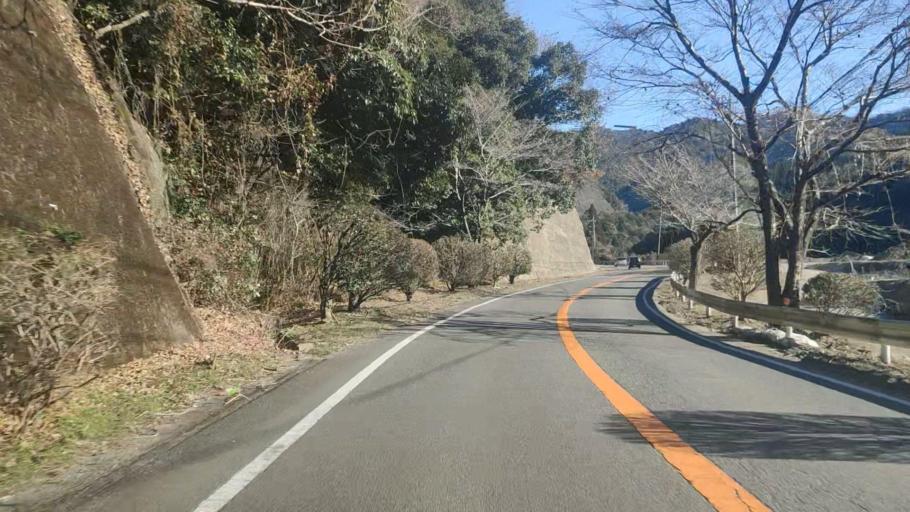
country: JP
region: Miyazaki
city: Nobeoka
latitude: 32.6233
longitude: 131.7093
